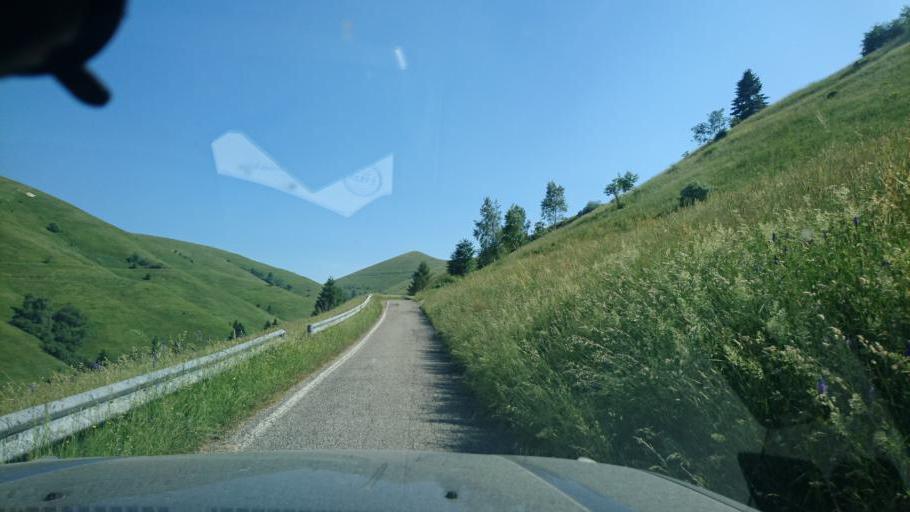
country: IT
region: Veneto
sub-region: Provincia di Treviso
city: Crespano del Grappa
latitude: 45.8905
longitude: 11.8349
